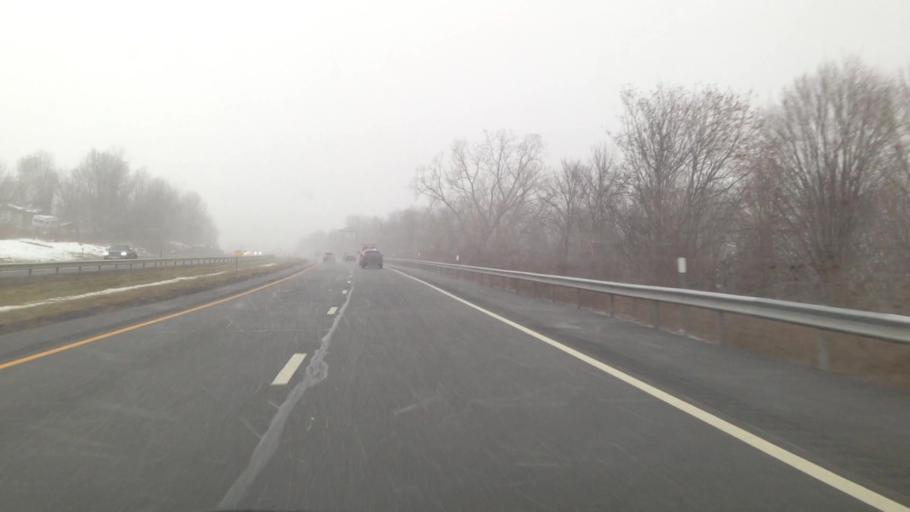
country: US
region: New York
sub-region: Montgomery County
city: Hagaman
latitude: 42.8915
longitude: -74.0858
